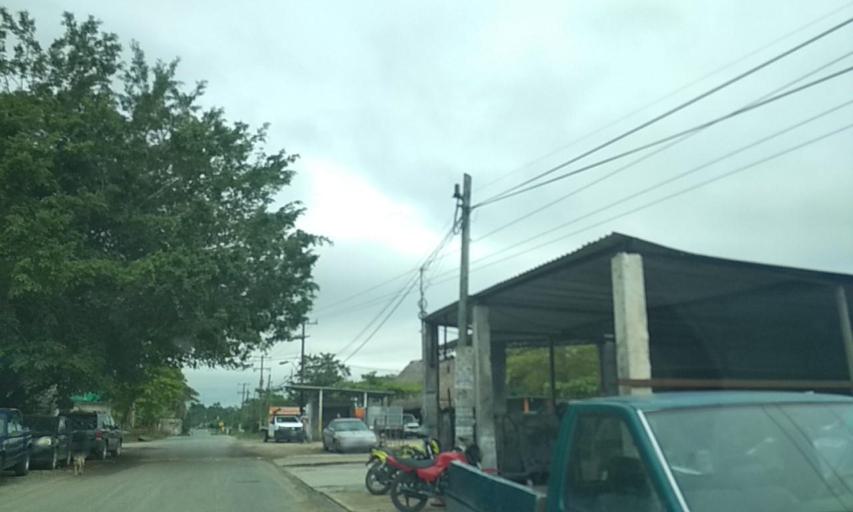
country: MX
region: Veracruz
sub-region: Uxpanapa
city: Poblado 10
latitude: 17.5051
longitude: -94.1608
